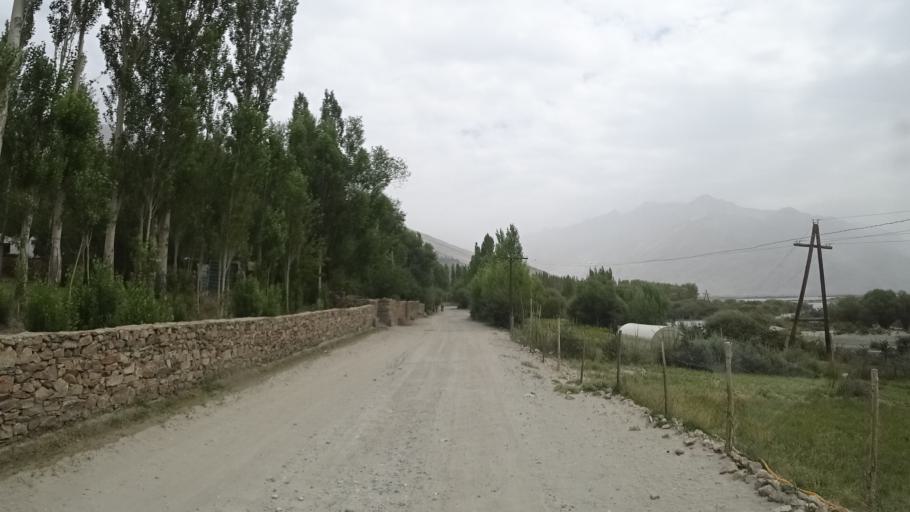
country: AF
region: Badakhshan
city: Khandud
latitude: 37.0283
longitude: 72.6146
